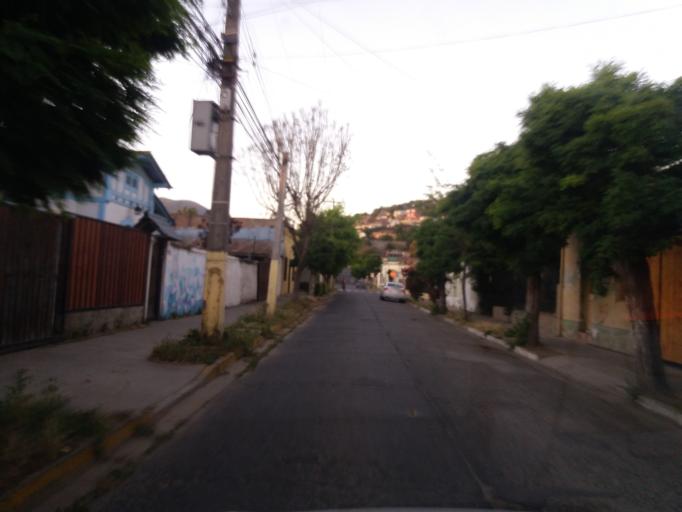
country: CL
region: Valparaiso
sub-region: Provincia de Quillota
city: Quillota
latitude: -32.8787
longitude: -71.2521
